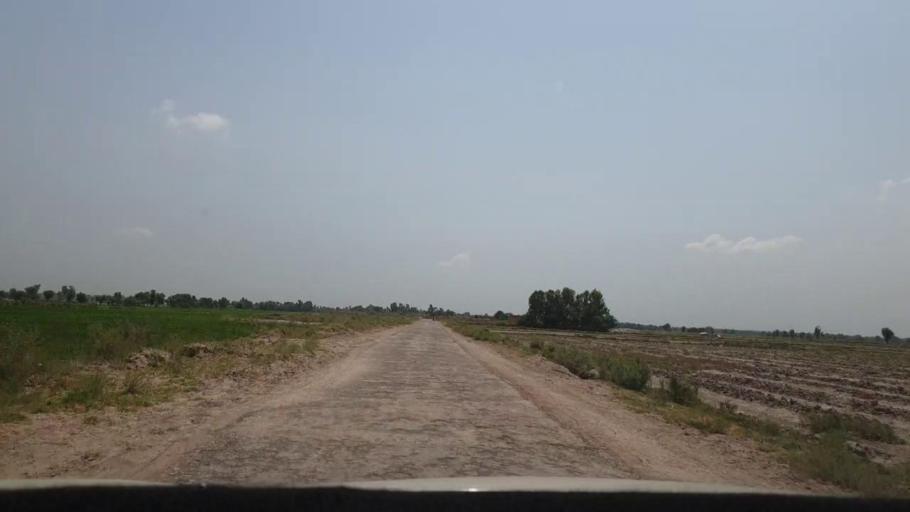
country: PK
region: Sindh
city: New Badah
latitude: 27.3004
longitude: 68.0605
